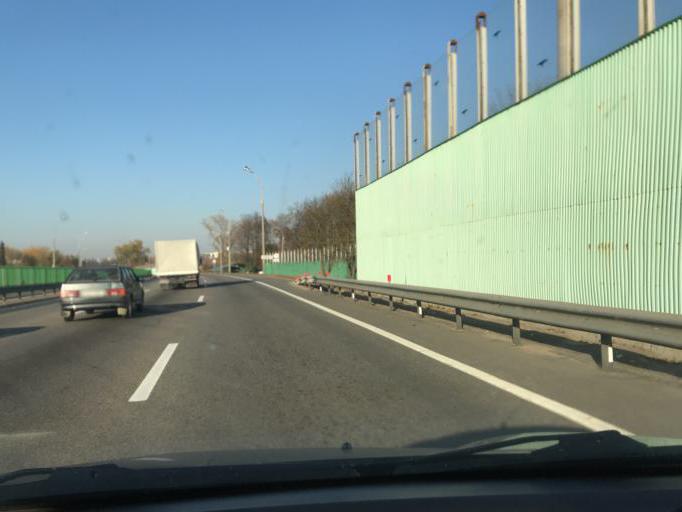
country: BY
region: Minsk
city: Syenitsa
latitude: 53.8236
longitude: 27.5334
